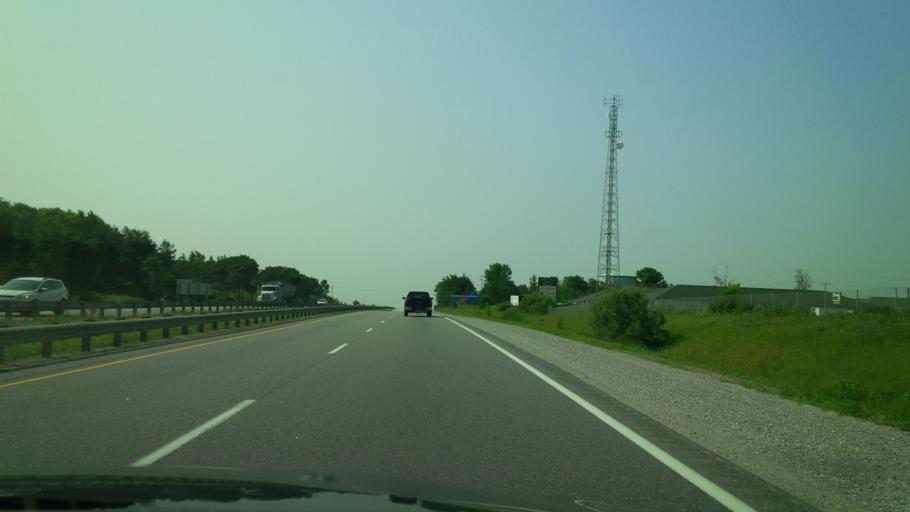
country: CA
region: Ontario
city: Orillia
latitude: 44.5980
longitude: -79.4476
